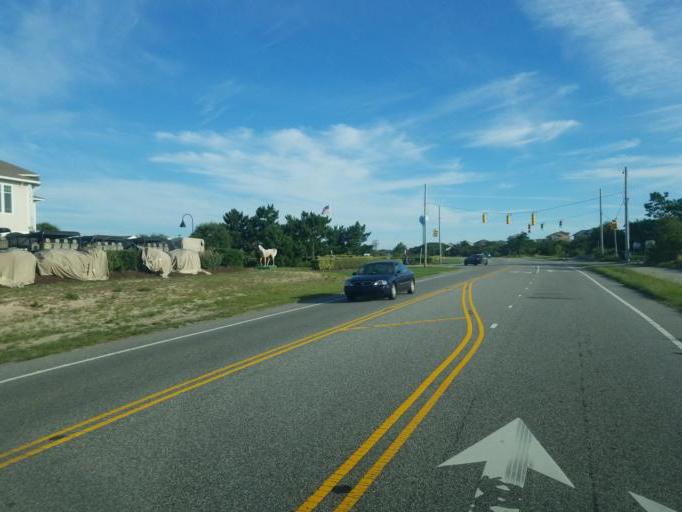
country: US
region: North Carolina
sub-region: Dare County
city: Southern Shores
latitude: 36.3012
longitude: -75.8043
